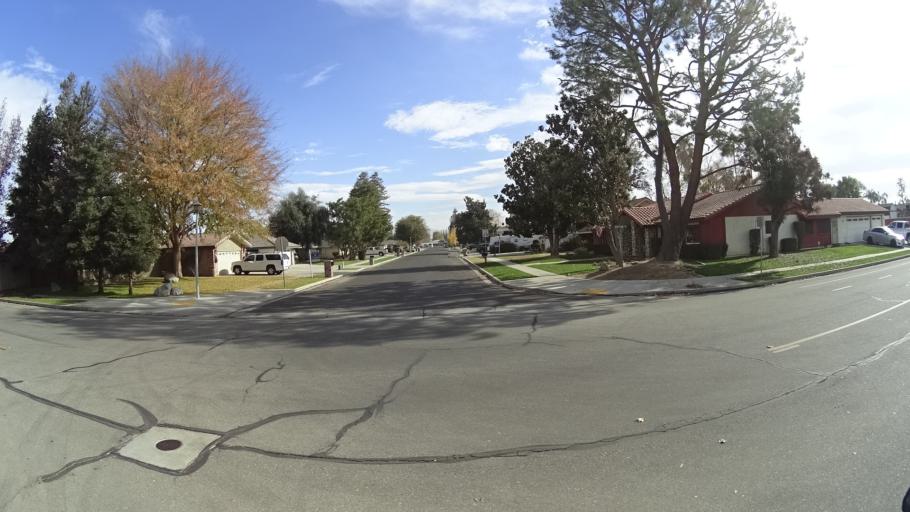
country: US
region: California
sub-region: Kern County
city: Greenacres
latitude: 35.4263
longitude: -119.0835
